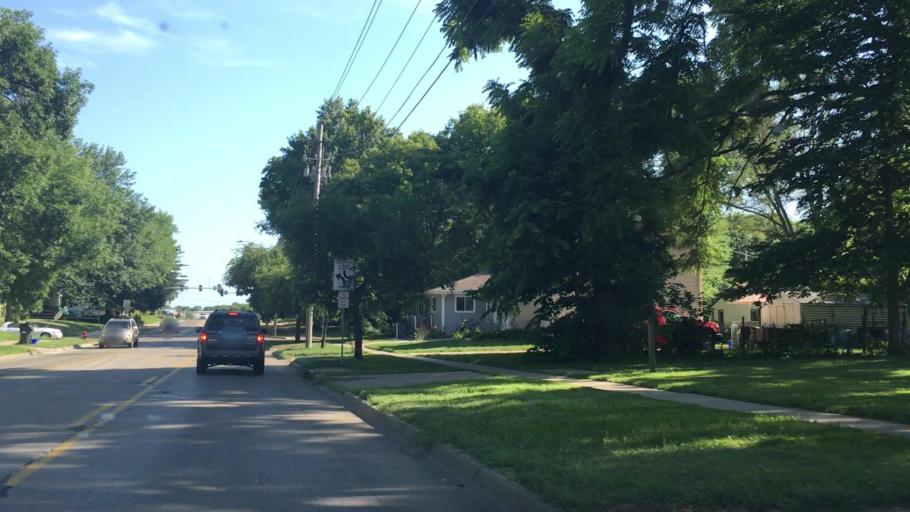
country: US
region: Iowa
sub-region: Johnson County
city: Iowa City
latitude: 41.6481
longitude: -91.5021
